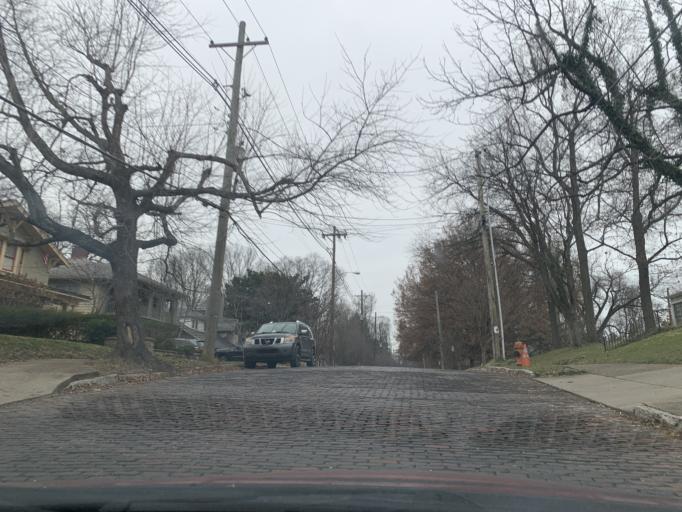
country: US
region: Kentucky
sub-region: Jefferson County
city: Indian Hills
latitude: 38.2500
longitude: -85.6973
